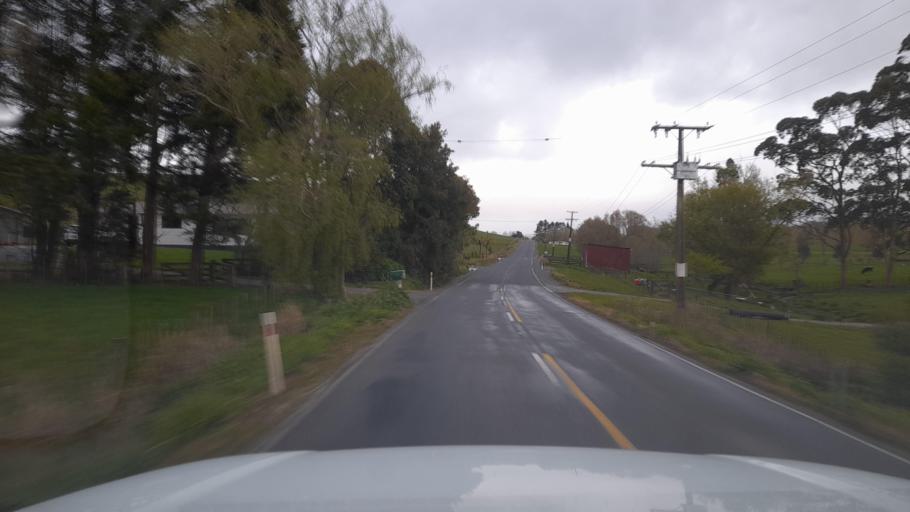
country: NZ
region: Northland
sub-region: Whangarei
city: Maungatapere
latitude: -35.7397
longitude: 174.1999
